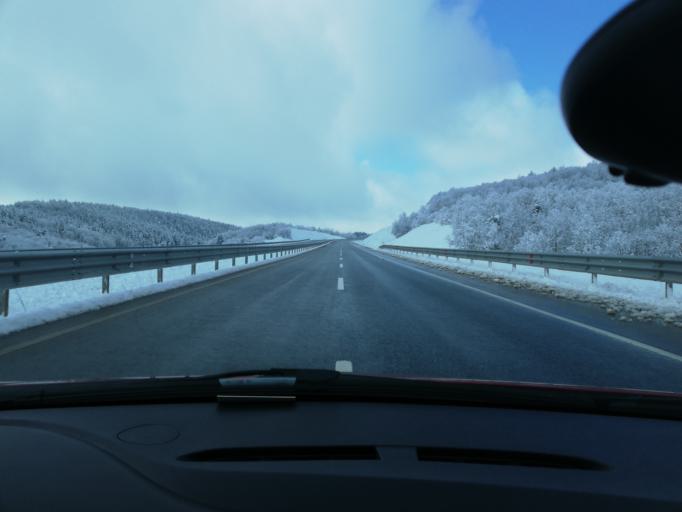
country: TR
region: Kastamonu
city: Ihsangazi
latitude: 41.3280
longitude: 33.6164
